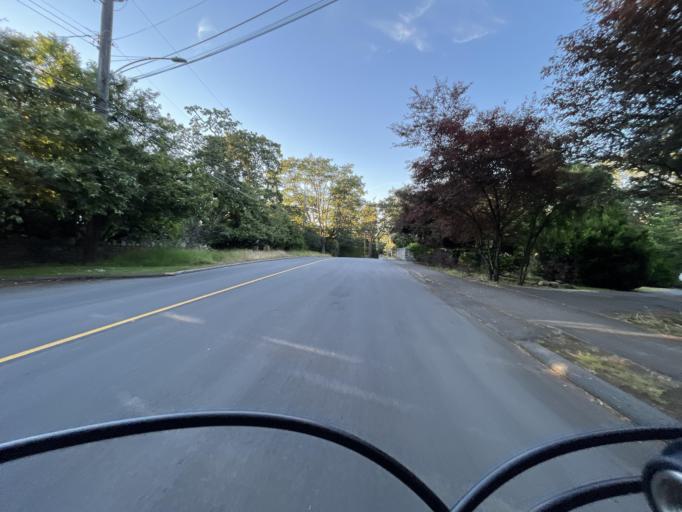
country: CA
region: British Columbia
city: Oak Bay
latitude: 48.4227
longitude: -123.3223
